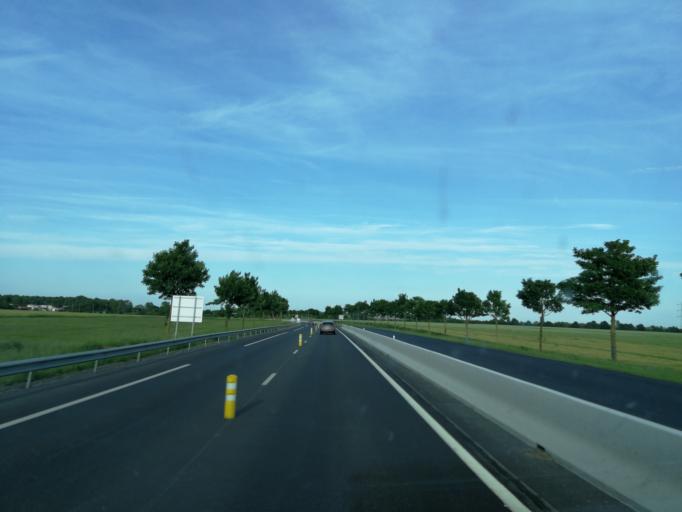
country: FR
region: Centre
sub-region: Departement d'Eure-et-Loir
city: Le Coudray
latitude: 48.4155
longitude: 1.4947
